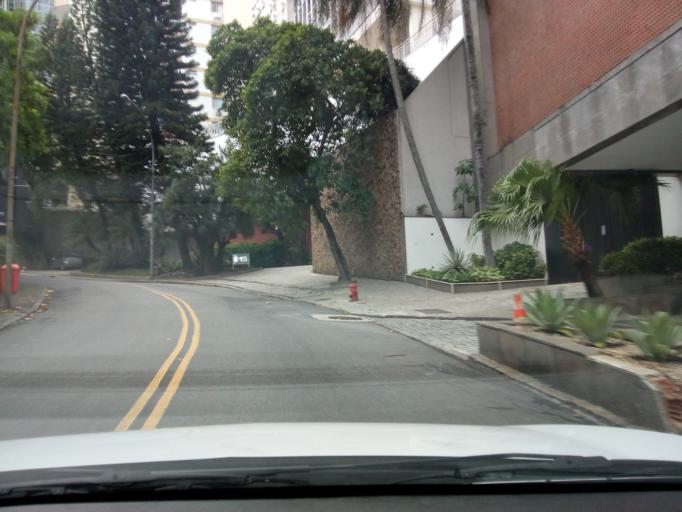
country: BR
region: Rio de Janeiro
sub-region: Rio De Janeiro
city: Rio de Janeiro
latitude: -22.9784
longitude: -43.1981
